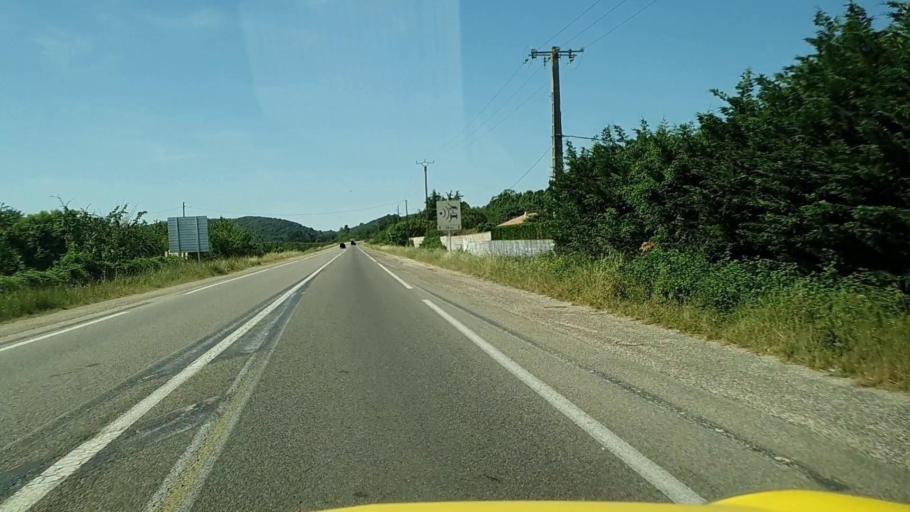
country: FR
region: Languedoc-Roussillon
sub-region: Departement du Gard
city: Connaux
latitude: 44.0860
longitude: 4.5942
